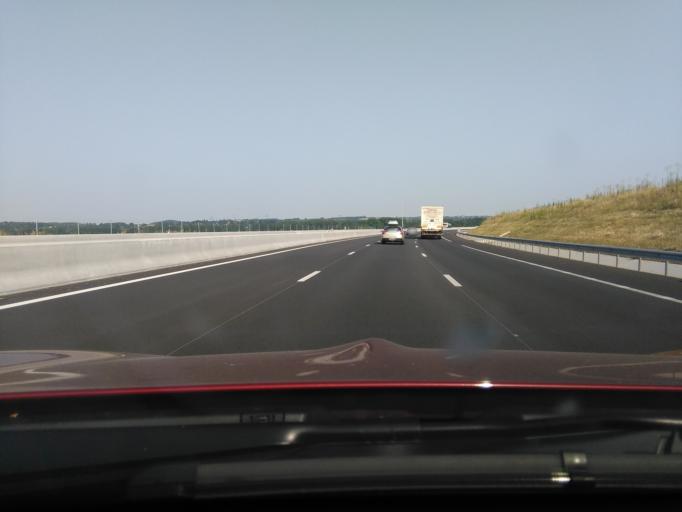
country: FR
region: Rhone-Alpes
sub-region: Departement du Rhone
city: Quincieux
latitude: 45.9166
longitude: 4.7886
